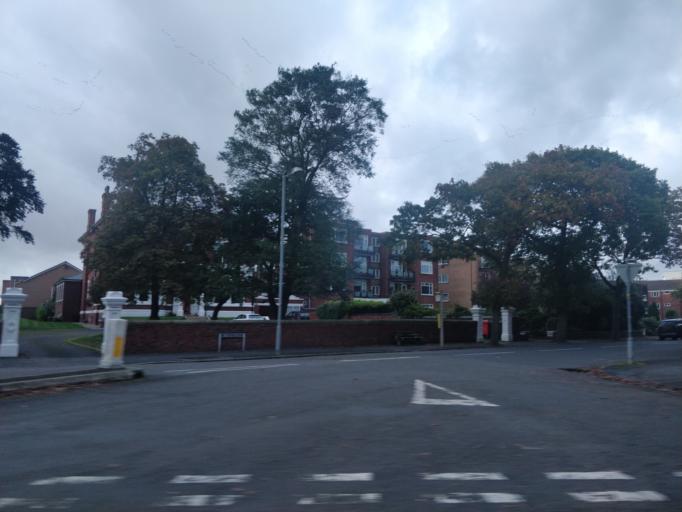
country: GB
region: England
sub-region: Sefton
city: Southport
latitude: 53.6583
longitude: -2.9872
